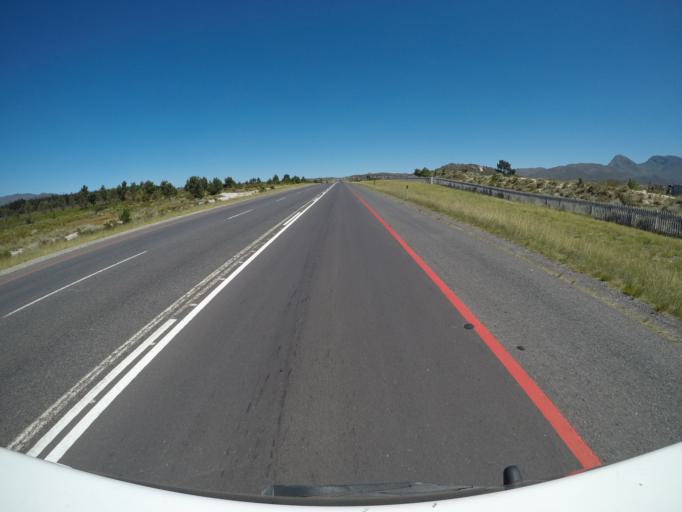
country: ZA
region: Western Cape
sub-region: Overberg District Municipality
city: Grabouw
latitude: -34.1643
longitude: 18.9911
